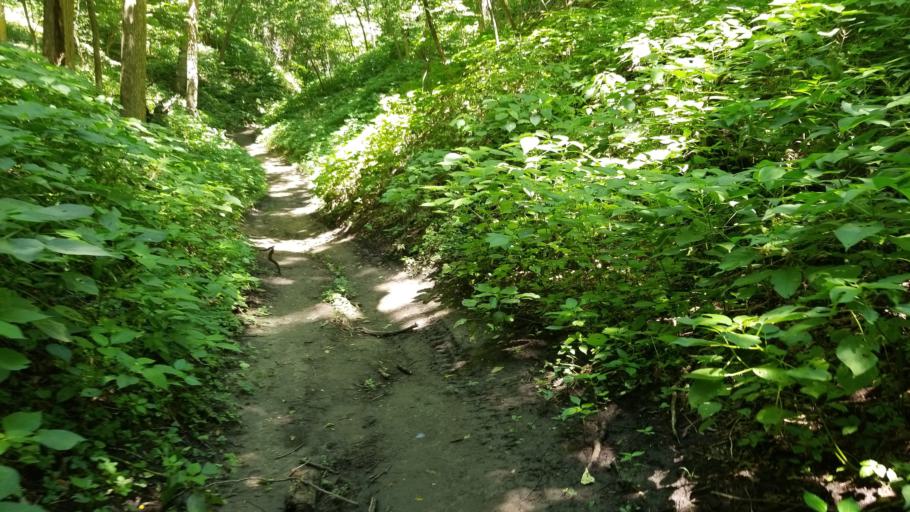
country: US
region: Iowa
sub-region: Pottawattamie County
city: Carter Lake
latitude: 41.3956
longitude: -95.9561
